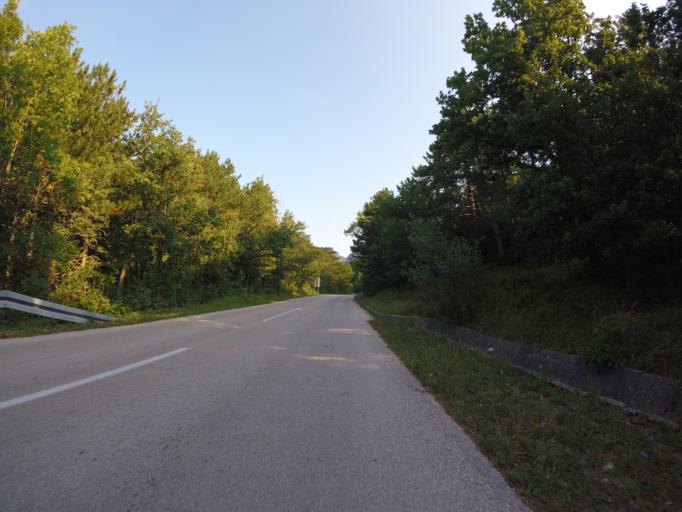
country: HR
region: Primorsko-Goranska
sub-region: Grad Crikvenica
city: Crikvenica
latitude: 45.2078
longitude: 14.7132
